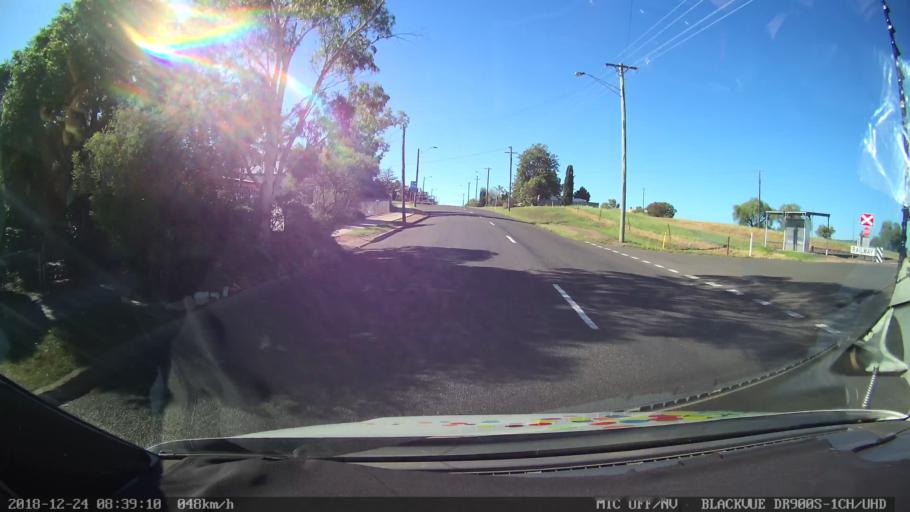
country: AU
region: New South Wales
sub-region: Liverpool Plains
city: Quirindi
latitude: -31.3461
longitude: 150.6473
